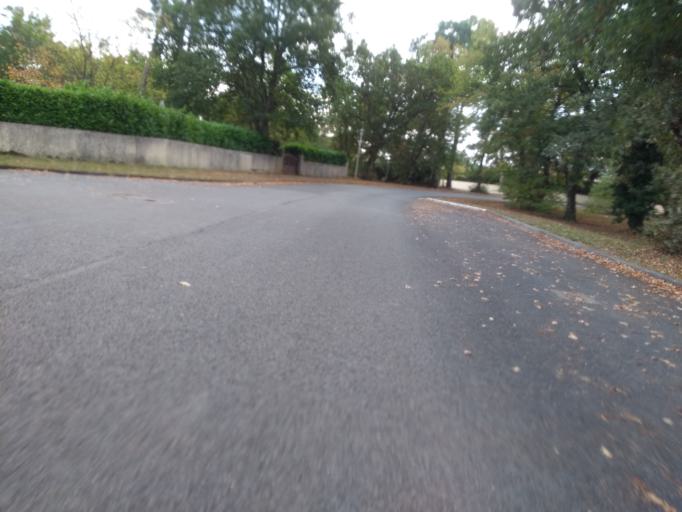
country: FR
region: Aquitaine
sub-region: Departement de la Gironde
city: Cestas
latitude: 44.7355
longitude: -0.6657
